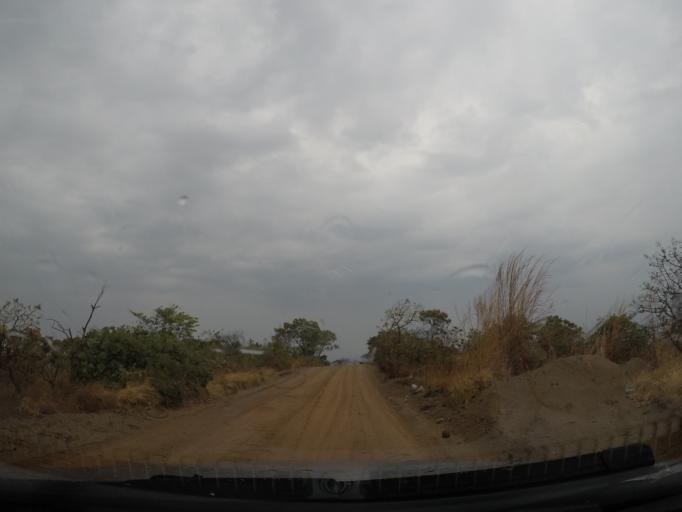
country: BR
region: Goias
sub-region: Pirenopolis
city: Pirenopolis
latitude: -15.8276
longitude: -48.9046
